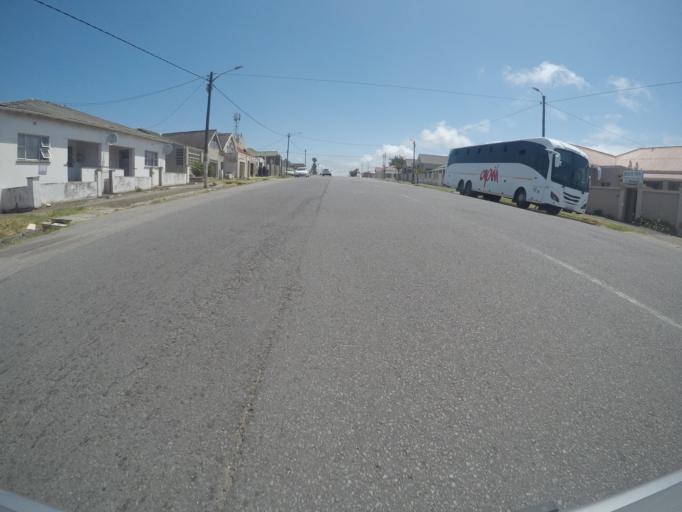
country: ZA
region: Eastern Cape
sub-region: Buffalo City Metropolitan Municipality
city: East London
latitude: -33.0125
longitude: 27.9175
